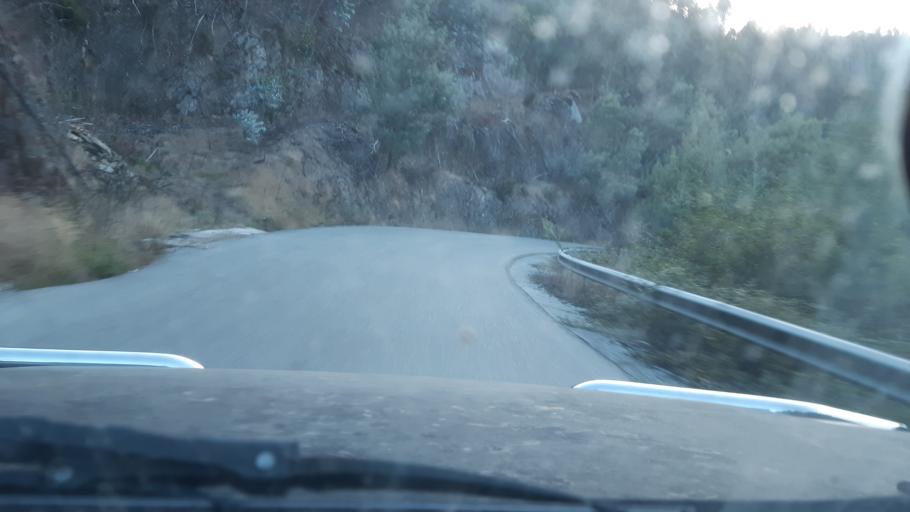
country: PT
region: Aveiro
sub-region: Agueda
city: Aguada de Cima
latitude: 40.5673
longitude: -8.3563
